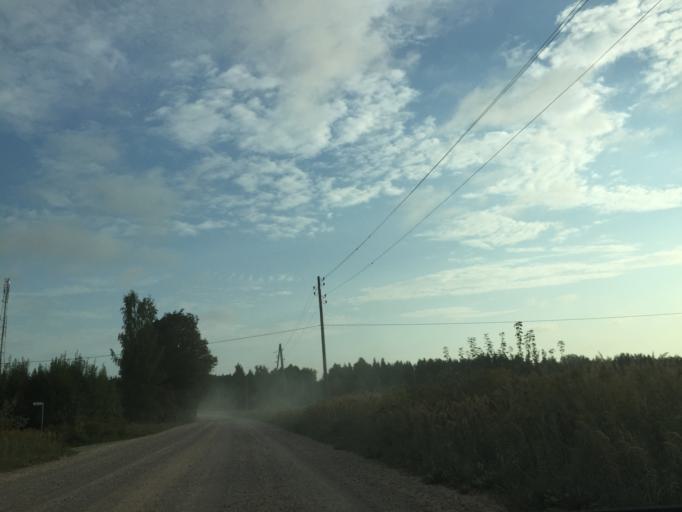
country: LV
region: Ikskile
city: Ikskile
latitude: 56.8143
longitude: 24.4480
